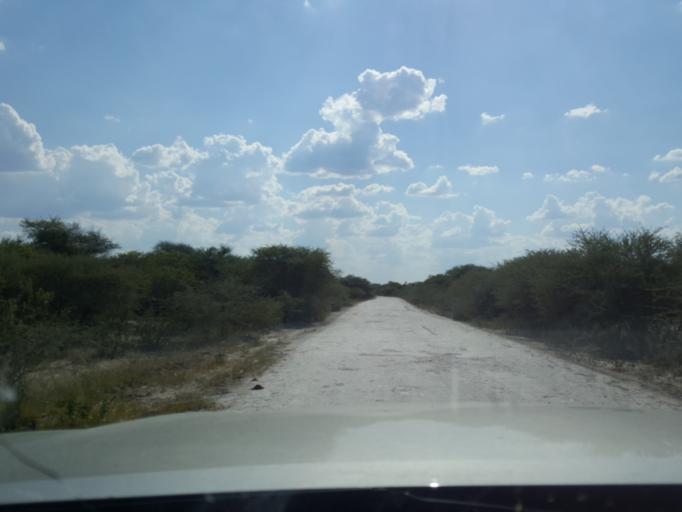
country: BW
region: North West
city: Shakawe
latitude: -18.7885
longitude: 21.7567
